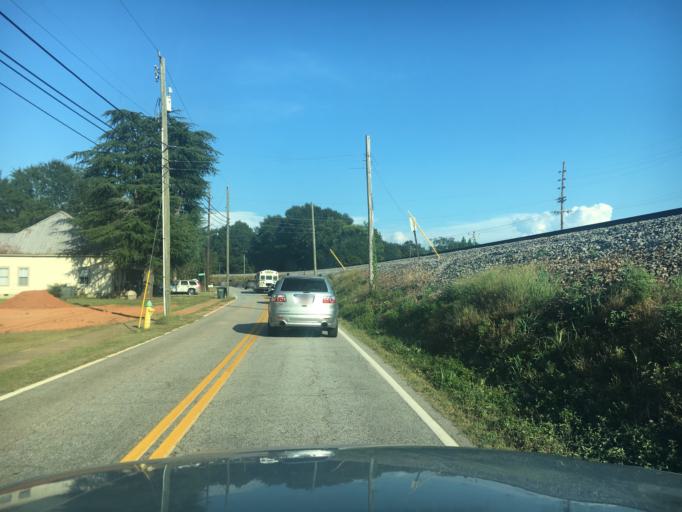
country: US
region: South Carolina
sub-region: Oconee County
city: Westminster
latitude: 34.6612
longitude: -83.0888
